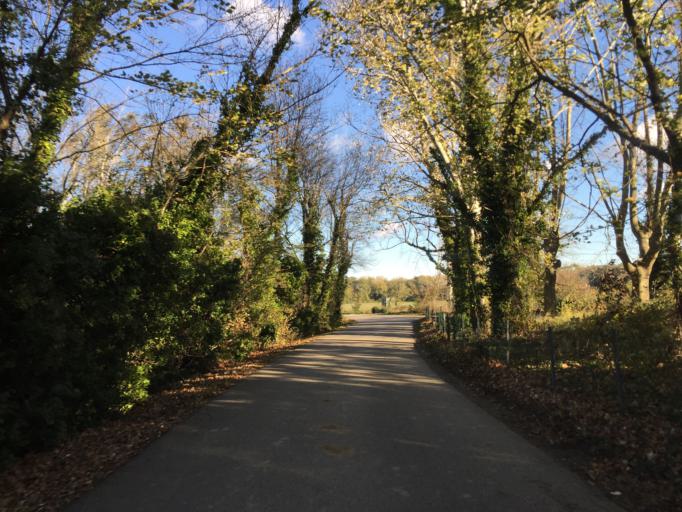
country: FR
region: Provence-Alpes-Cote d'Azur
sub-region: Departement du Vaucluse
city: Chateauneuf-du-Pape
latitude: 44.0215
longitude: 4.8343
